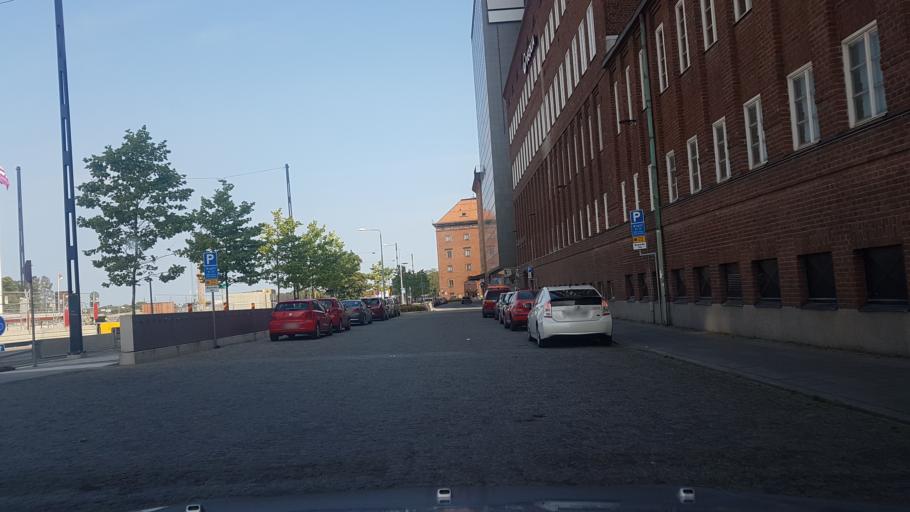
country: SE
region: Stockholm
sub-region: Stockholms Kommun
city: Stockholm
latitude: 59.3470
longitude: 18.0367
